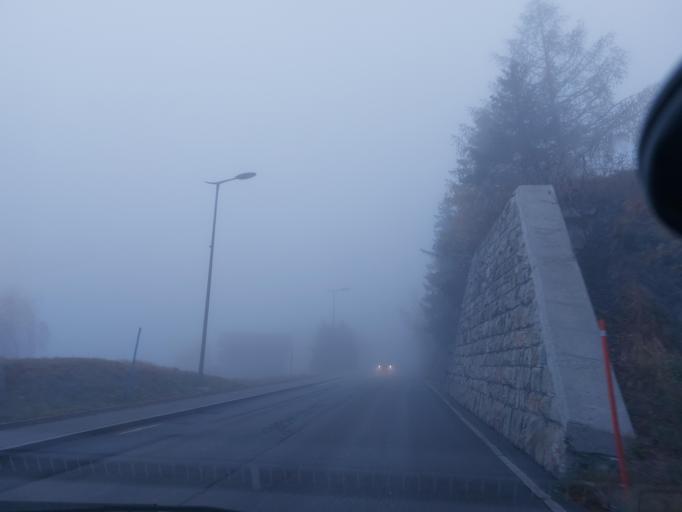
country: CH
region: Valais
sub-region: Sierre District
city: Lens
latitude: 46.3009
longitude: 7.4523
